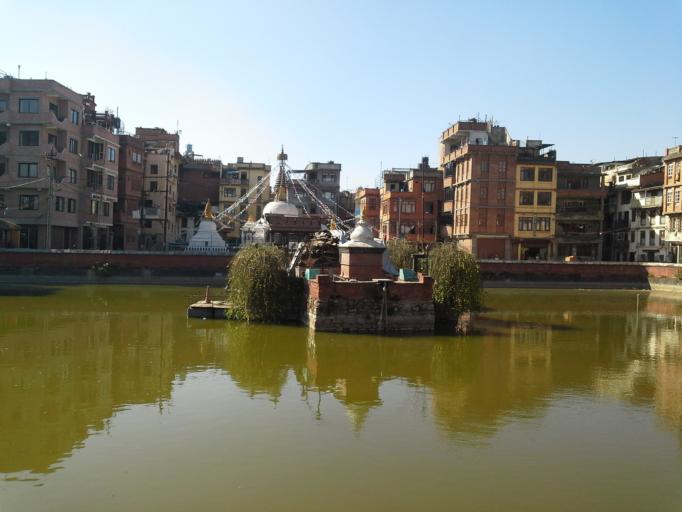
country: NP
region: Central Region
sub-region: Bagmati Zone
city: Patan
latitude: 27.6759
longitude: 85.3213
